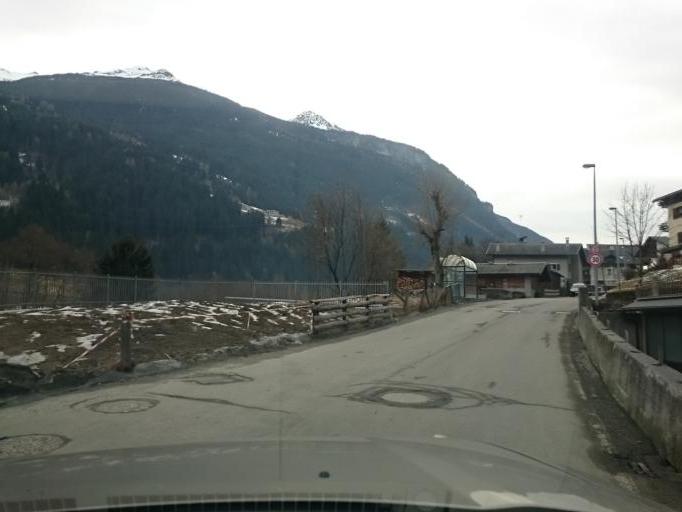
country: IT
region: Lombardy
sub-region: Provincia di Sondrio
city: Cepina
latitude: 46.4390
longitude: 10.3564
